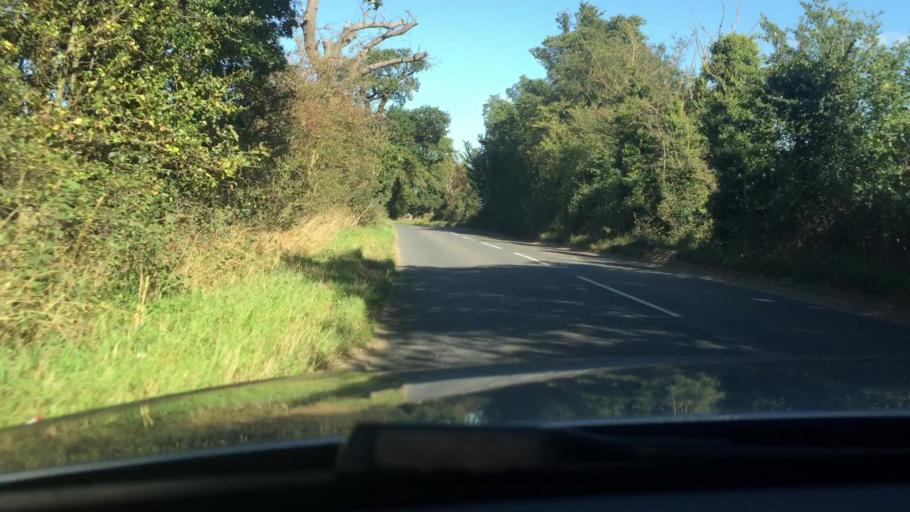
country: GB
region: England
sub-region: Suffolk
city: Kesgrave
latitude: 52.0488
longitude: 1.2867
